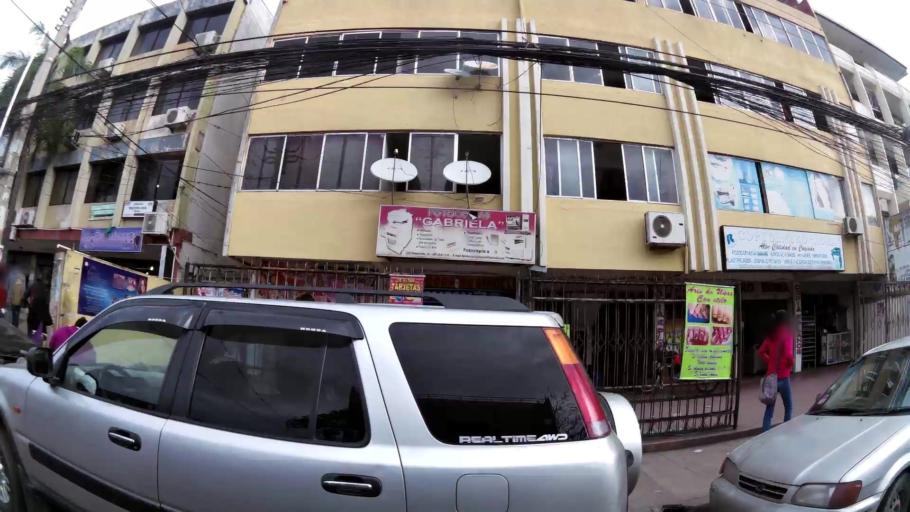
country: BO
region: Santa Cruz
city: Santa Cruz de la Sierra
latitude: -17.7782
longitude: -63.1891
